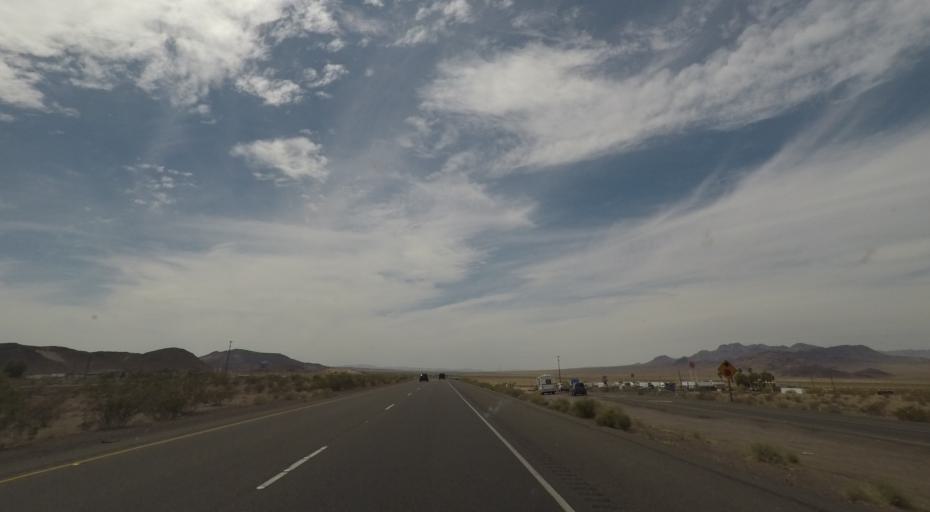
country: US
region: California
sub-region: San Bernardino County
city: Twentynine Palms
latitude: 34.7259
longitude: -116.1593
